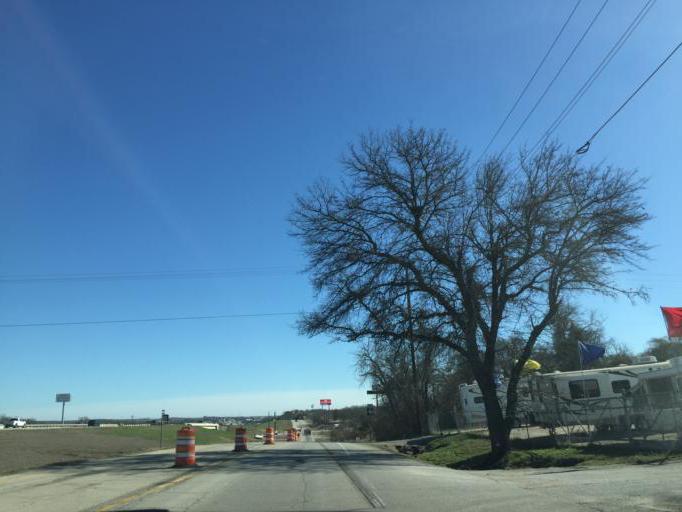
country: US
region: Texas
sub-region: Parker County
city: Willow Park
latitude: 32.7480
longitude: -97.6768
